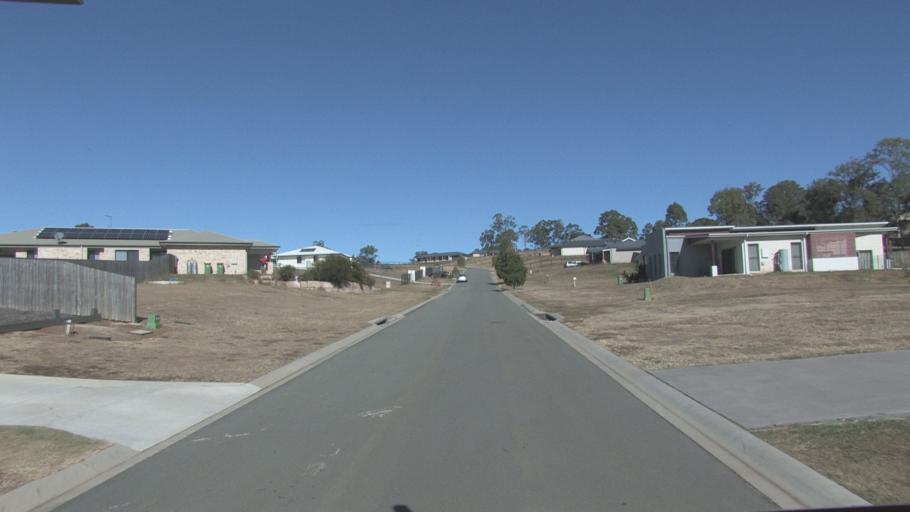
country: AU
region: Queensland
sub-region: Logan
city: Cedar Vale
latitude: -27.8879
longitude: 152.9818
